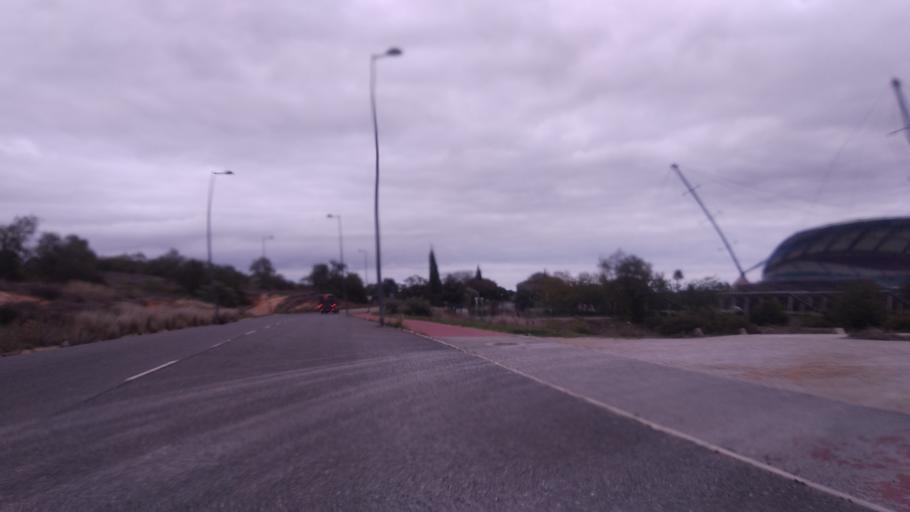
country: PT
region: Faro
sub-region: Faro
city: Santa Barbara de Nexe
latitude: 37.0910
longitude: -7.9767
